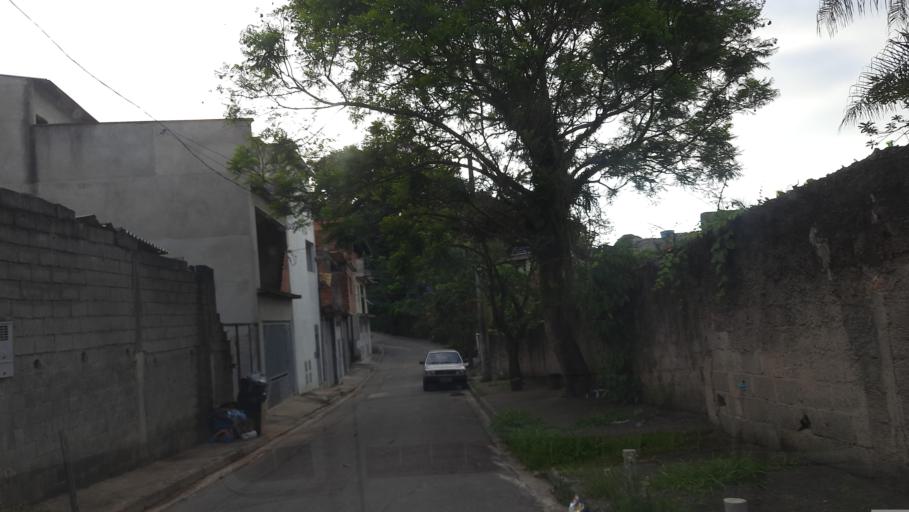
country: BR
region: Sao Paulo
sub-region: Caieiras
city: Caieiras
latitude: -23.4345
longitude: -46.7094
